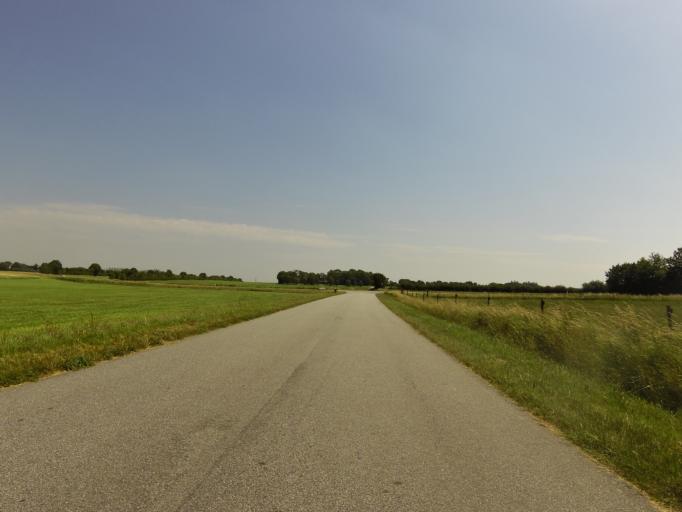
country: DK
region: South Denmark
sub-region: Haderslev Kommune
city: Vojens
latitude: 55.1577
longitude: 9.2594
